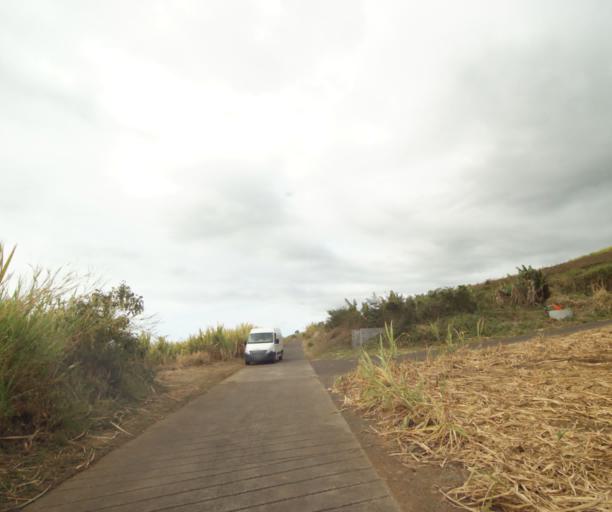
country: RE
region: Reunion
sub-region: Reunion
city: Saint-Paul
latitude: -21.0274
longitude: 55.3193
